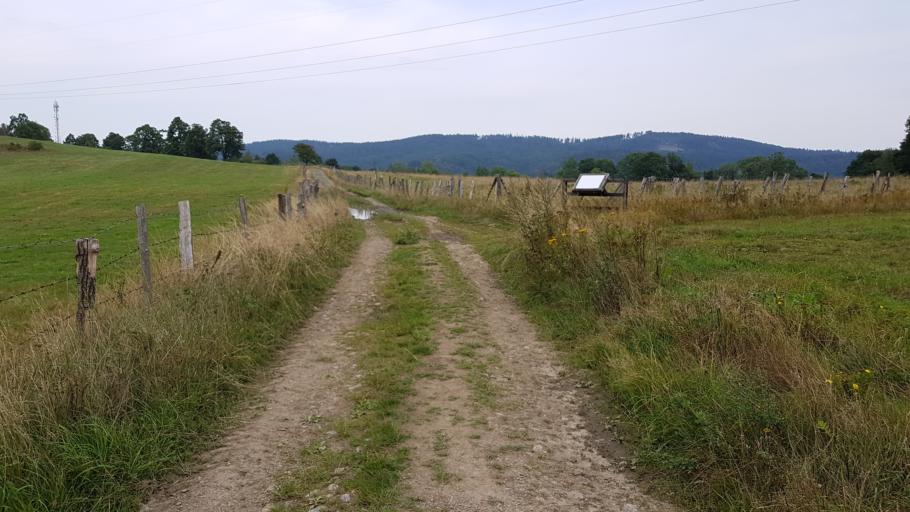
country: PL
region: Lower Silesian Voivodeship
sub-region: Powiat jeleniogorski
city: Janowice Wielkie
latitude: 50.8691
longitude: 15.9476
